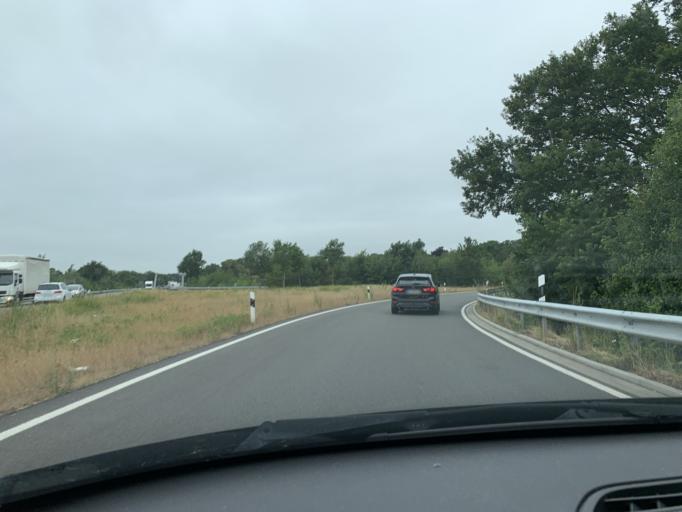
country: DE
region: Lower Saxony
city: Lingen
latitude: 52.4935
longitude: 7.3005
